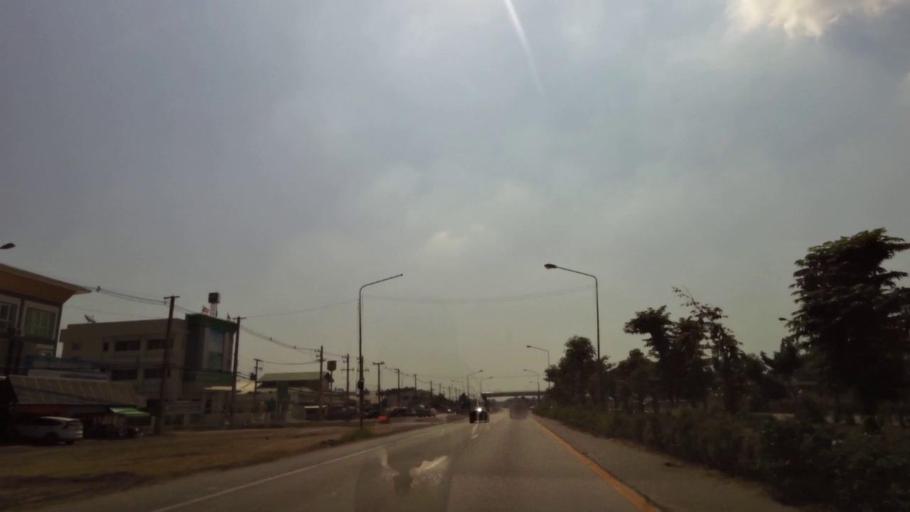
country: TH
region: Phichit
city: Wachira Barami
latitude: 16.5269
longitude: 100.1432
